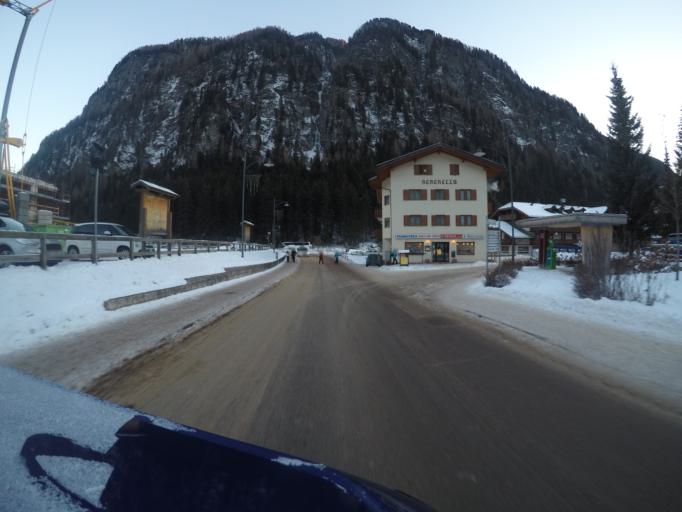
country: IT
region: Trentino-Alto Adige
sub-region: Provincia di Trento
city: Campitello di Fassa
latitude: 46.4752
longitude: 11.7440
